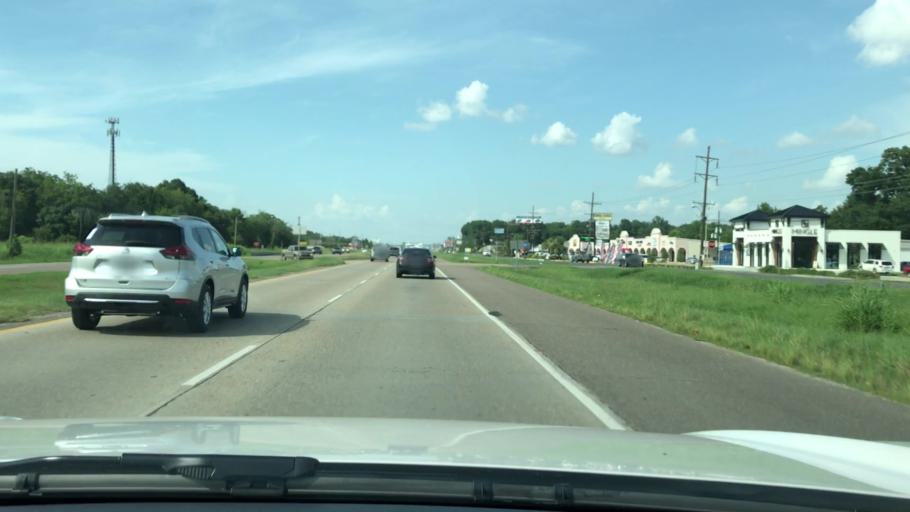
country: US
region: Louisiana
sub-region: West Baton Rouge Parish
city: Brusly
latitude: 30.4076
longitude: -91.2294
